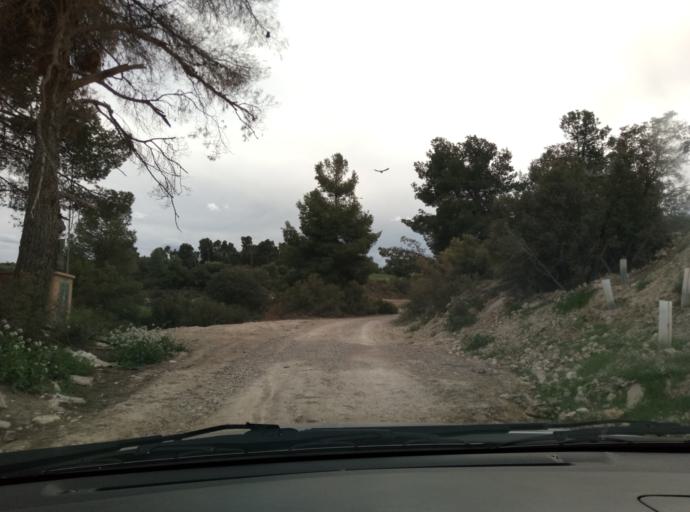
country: ES
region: Catalonia
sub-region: Provincia de Lleida
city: Nalec
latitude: 41.5813
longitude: 1.1138
